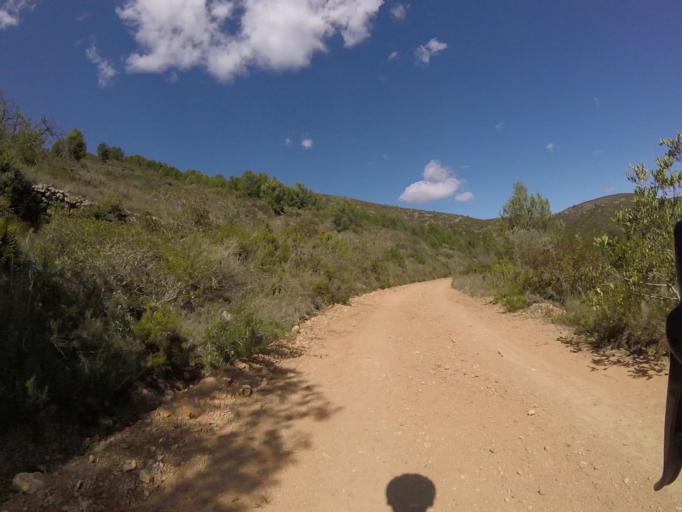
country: ES
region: Valencia
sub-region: Provincia de Castello
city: Cabanes
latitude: 40.1620
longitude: 0.1132
